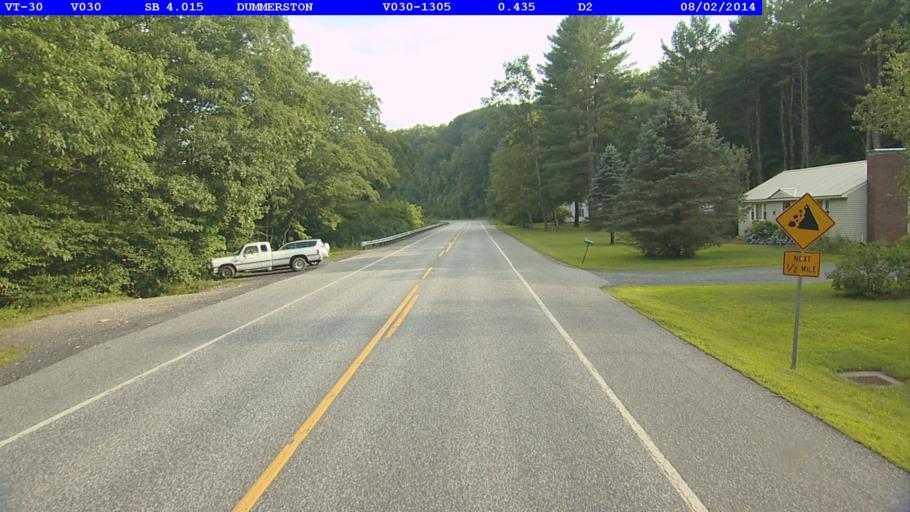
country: US
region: Vermont
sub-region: Windham County
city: West Brattleboro
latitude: 42.9031
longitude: -72.6011
